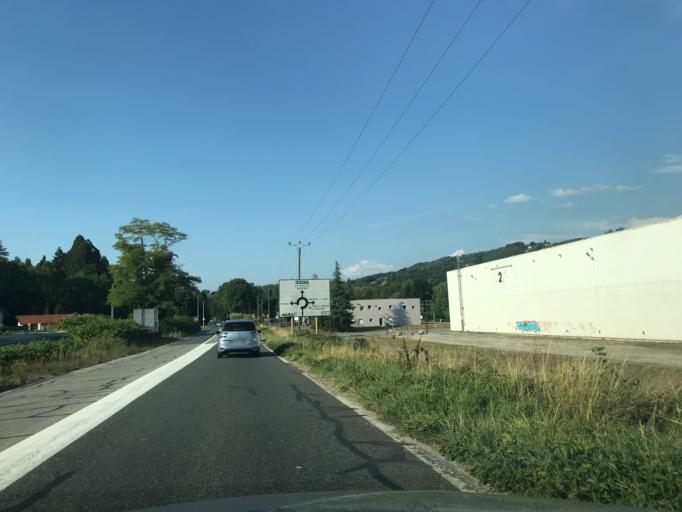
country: FR
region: Rhone-Alpes
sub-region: Departement de la Savoie
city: Gresy-sur-Aix
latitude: 45.7245
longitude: 5.9191
